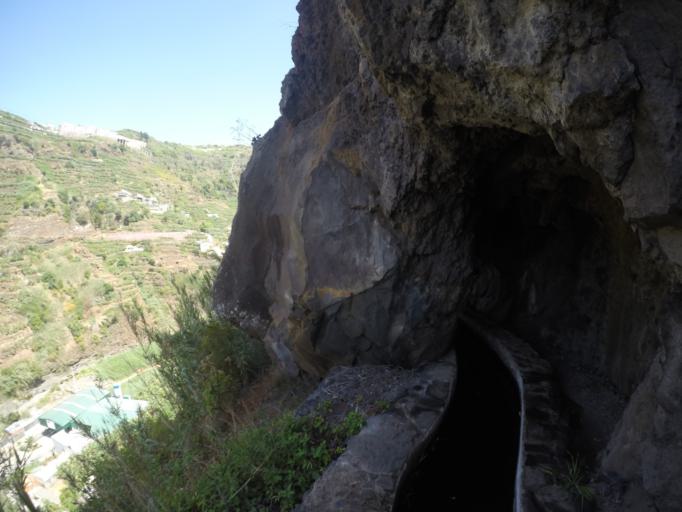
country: PT
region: Madeira
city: Camara de Lobos
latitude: 32.6630
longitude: -16.9590
